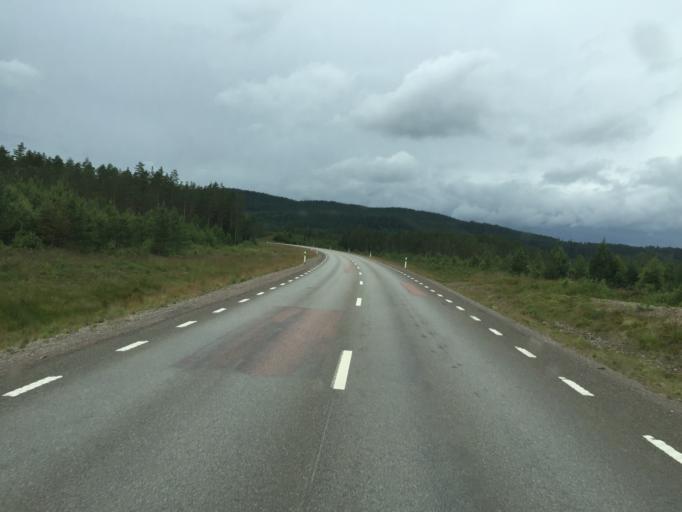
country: SE
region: Dalarna
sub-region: Malung-Saelens kommun
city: Malung
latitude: 60.6483
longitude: 13.6404
